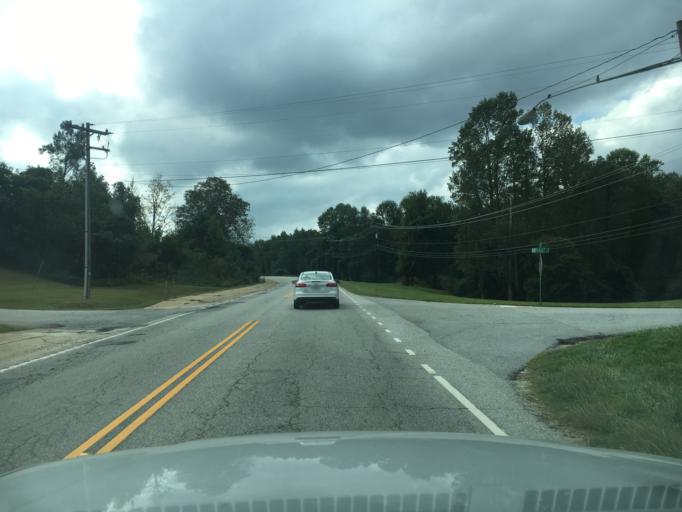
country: US
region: South Carolina
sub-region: Spartanburg County
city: Landrum
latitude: 35.1709
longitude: -82.1948
